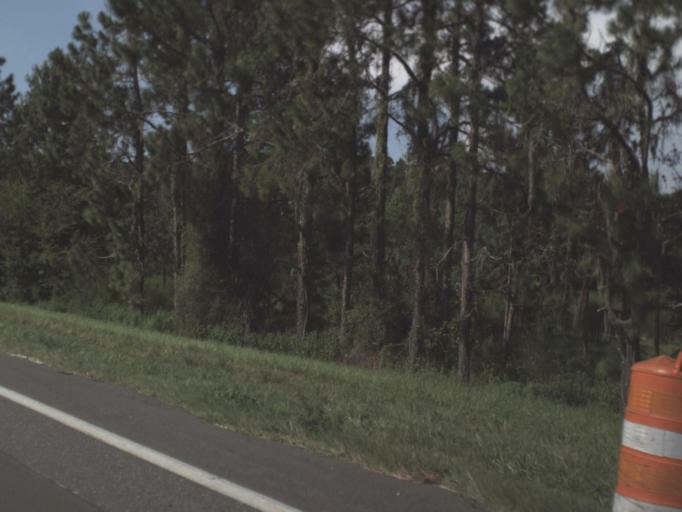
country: US
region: Florida
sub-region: Hillsborough County
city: Pebble Creek
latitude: 28.1606
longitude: -82.3944
